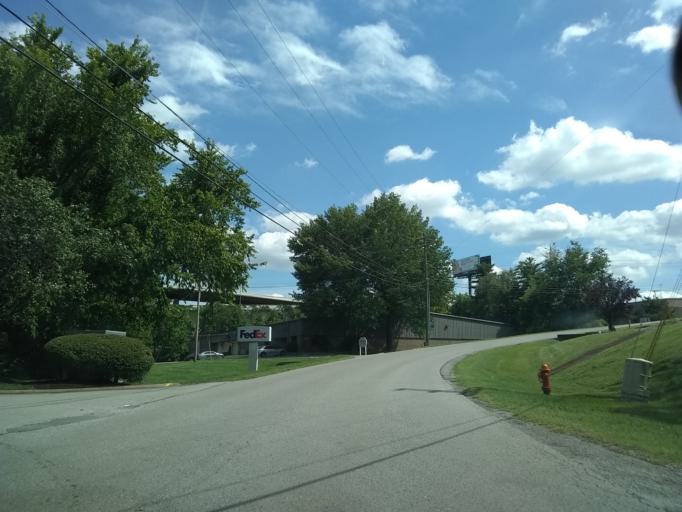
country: US
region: Tennessee
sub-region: Davidson County
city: Nashville
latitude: 36.1472
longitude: -86.6972
